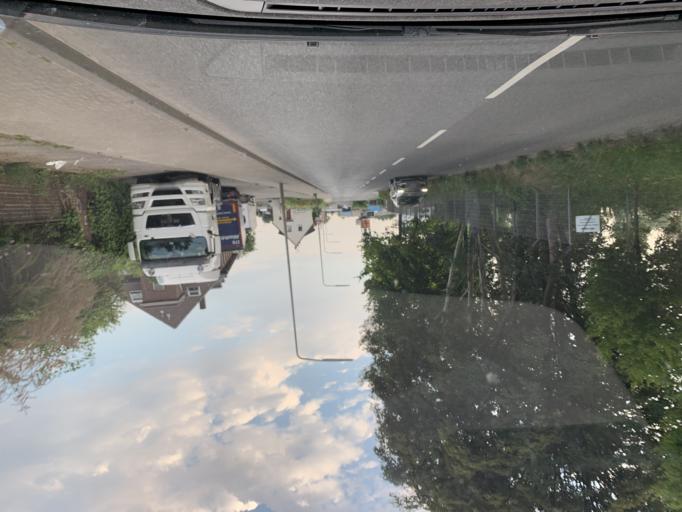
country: DE
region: North Rhine-Westphalia
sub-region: Regierungsbezirk Dusseldorf
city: Dusseldorf
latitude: 51.2190
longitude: 6.7427
